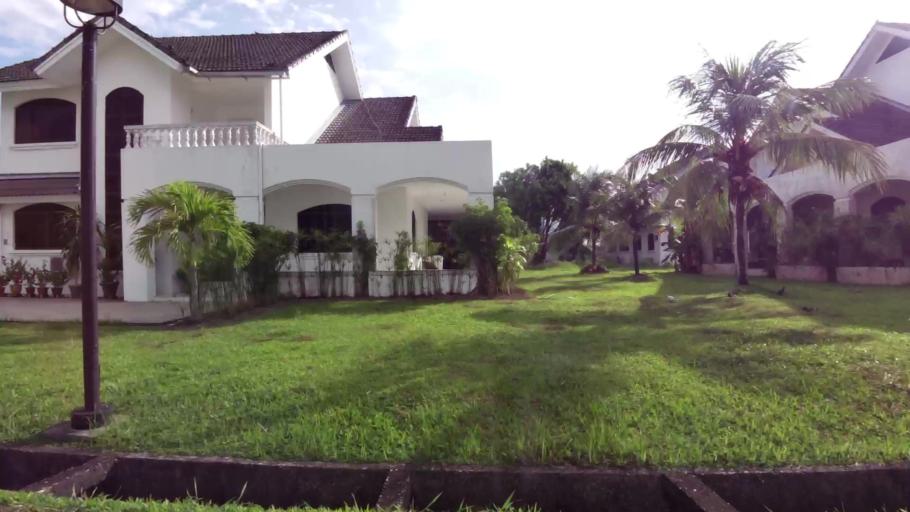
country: BN
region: Brunei and Muara
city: Bandar Seri Begawan
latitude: 4.9633
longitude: 114.9722
